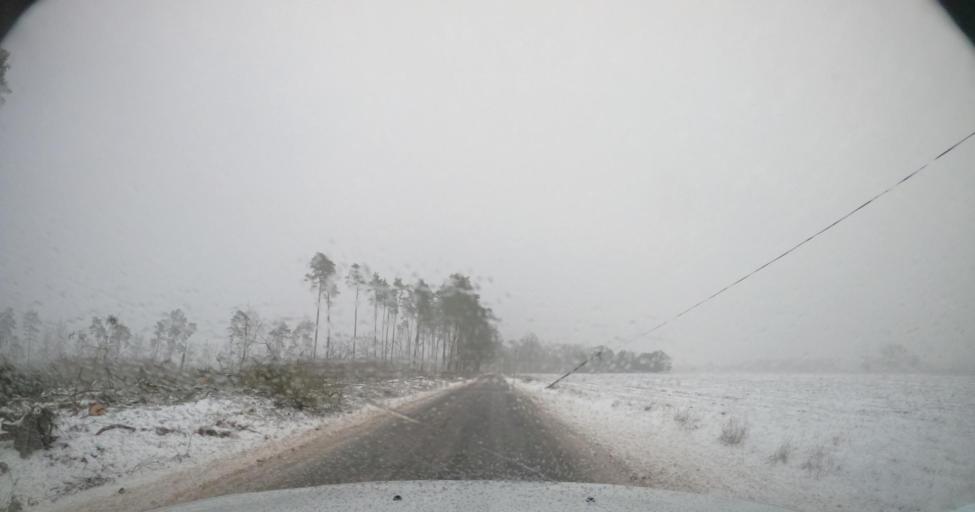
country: PL
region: West Pomeranian Voivodeship
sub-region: Powiat goleniowski
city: Przybiernow
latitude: 53.6881
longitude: 14.8464
